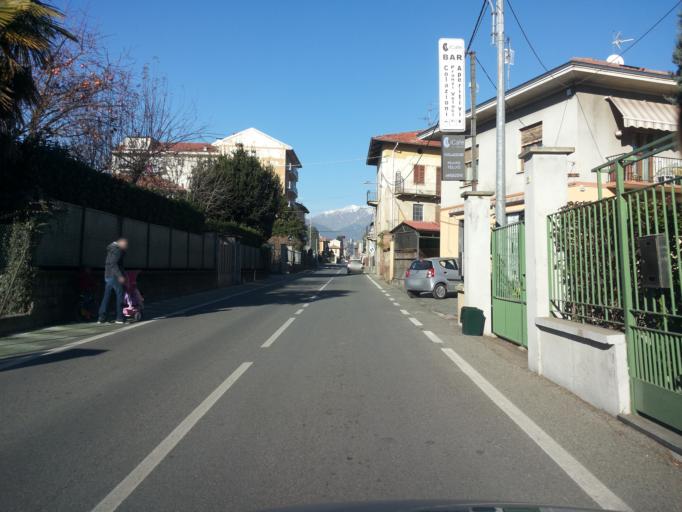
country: IT
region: Piedmont
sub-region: Provincia di Biella
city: Ponderano
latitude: 45.5417
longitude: 8.0534
